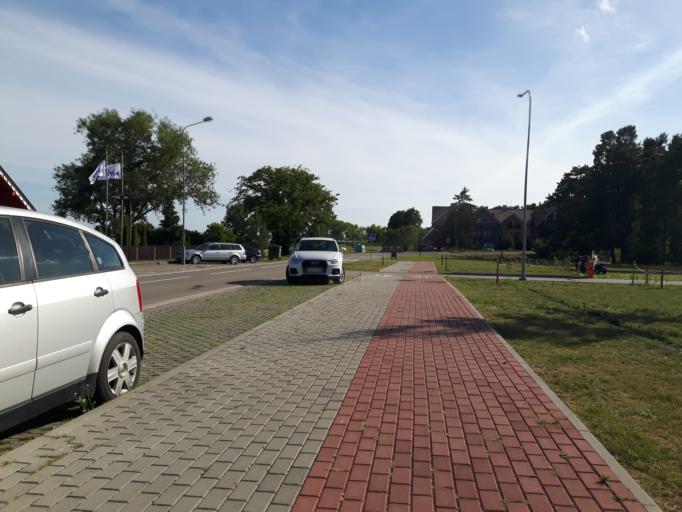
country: LT
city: Nida
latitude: 55.3173
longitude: 21.0194
